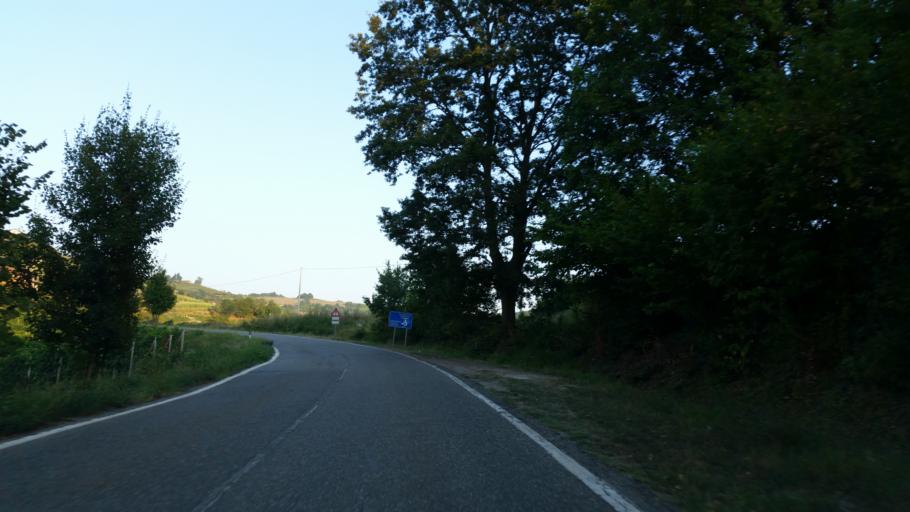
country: IT
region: Piedmont
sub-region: Provincia di Cuneo
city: Trezzo Tinella
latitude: 44.6580
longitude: 8.0952
